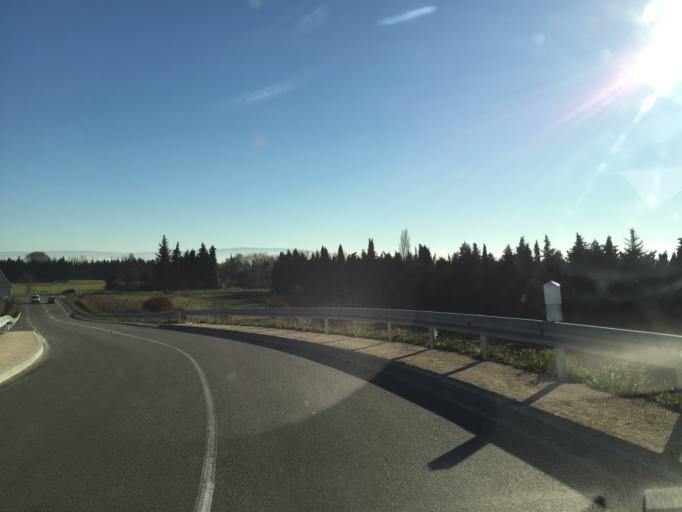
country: FR
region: Provence-Alpes-Cote d'Azur
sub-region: Departement du Vaucluse
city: Entraigues-sur-la-Sorgue
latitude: 44.0100
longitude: 4.9352
